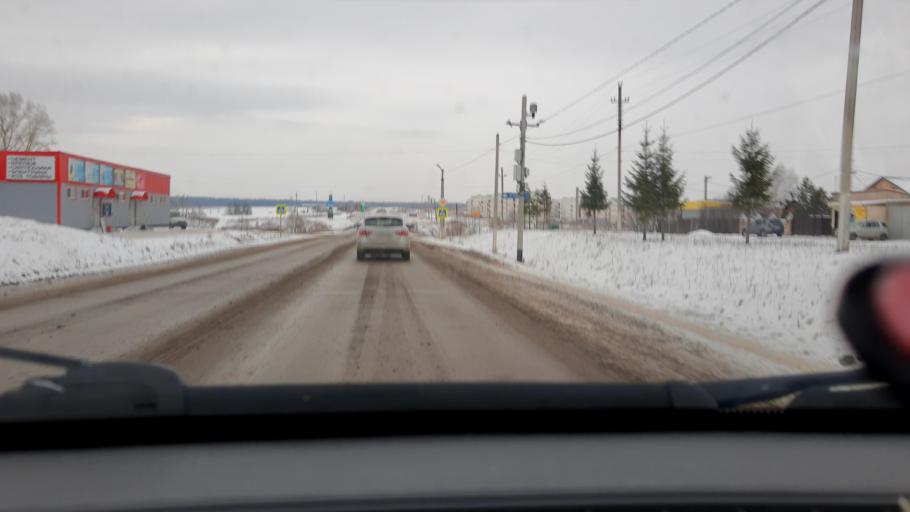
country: RU
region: Bashkortostan
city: Iglino
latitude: 54.8063
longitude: 56.4117
